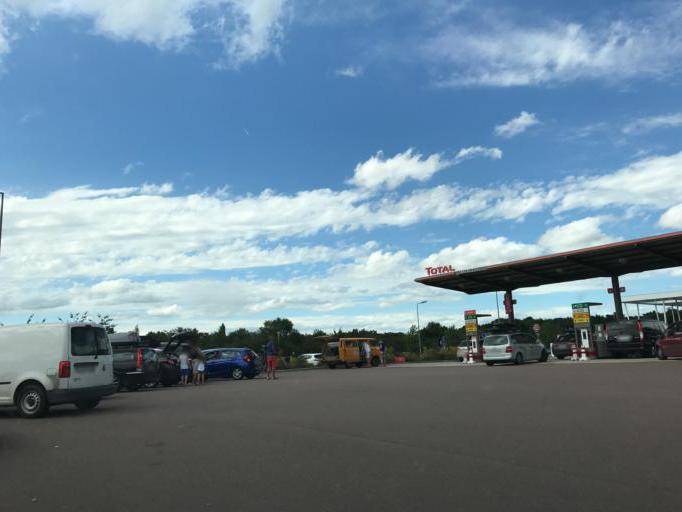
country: FR
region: Bourgogne
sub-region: Departement de la Cote-d'Or
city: Bligny-les-Beaune
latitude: 46.9621
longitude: 4.8378
